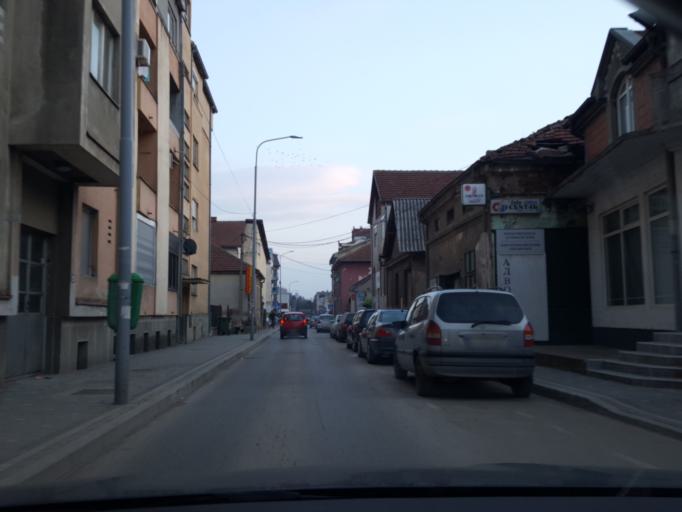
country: RS
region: Central Serbia
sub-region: Nisavski Okrug
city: Aleksinac
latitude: 43.5400
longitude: 21.7081
